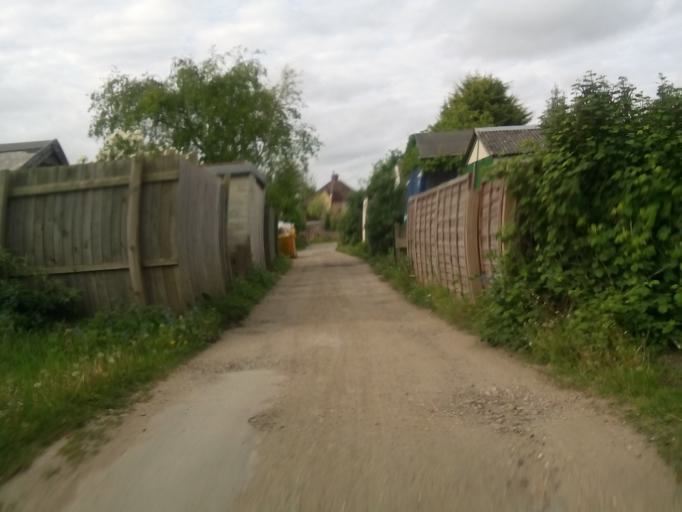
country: GB
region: England
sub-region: Cambridgeshire
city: Cambridge
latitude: 52.2034
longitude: 0.1480
